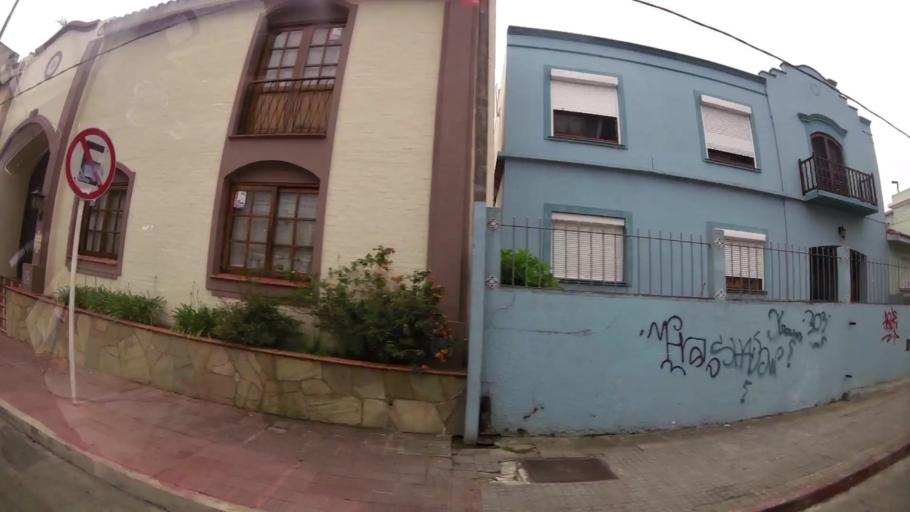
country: UY
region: Maldonado
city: Maldonado
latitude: -34.9127
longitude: -54.9591
